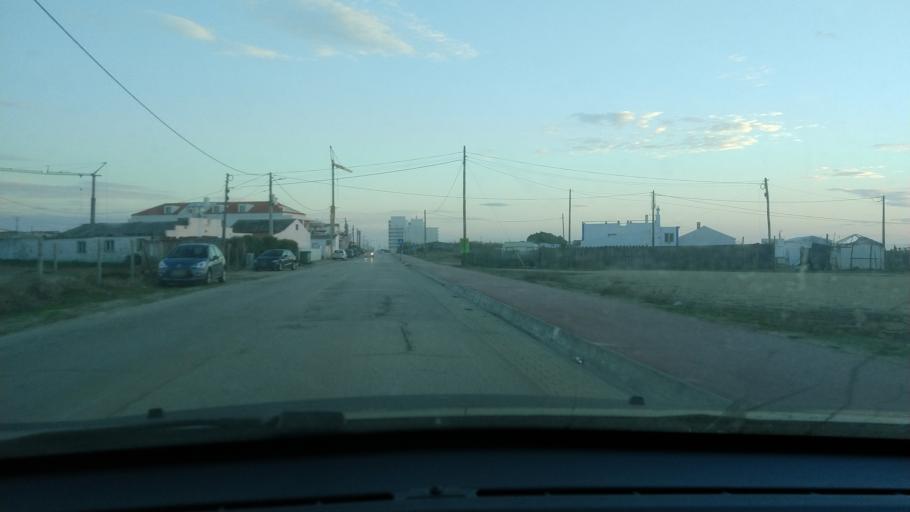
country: PT
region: Leiria
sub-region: Peniche
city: Atouguia da Baleia
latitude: 39.3698
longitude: -9.3367
